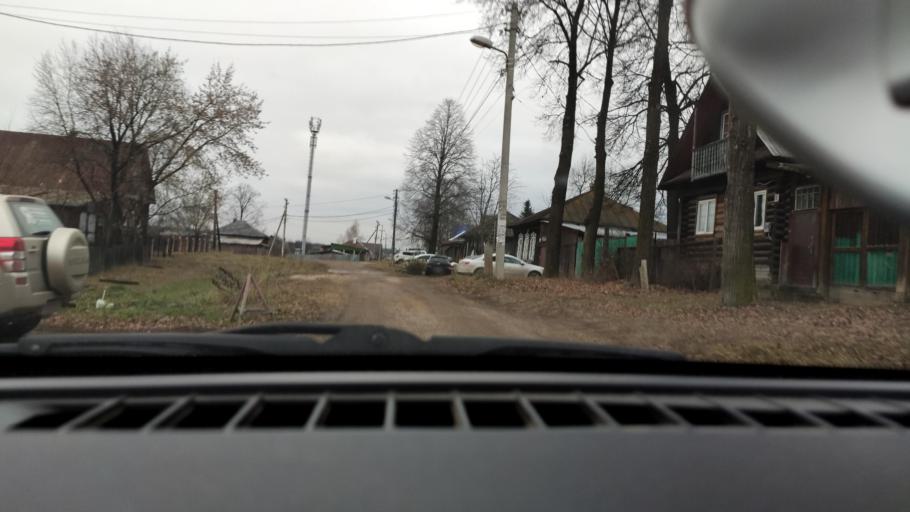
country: RU
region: Perm
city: Perm
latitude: 58.0285
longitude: 56.3356
